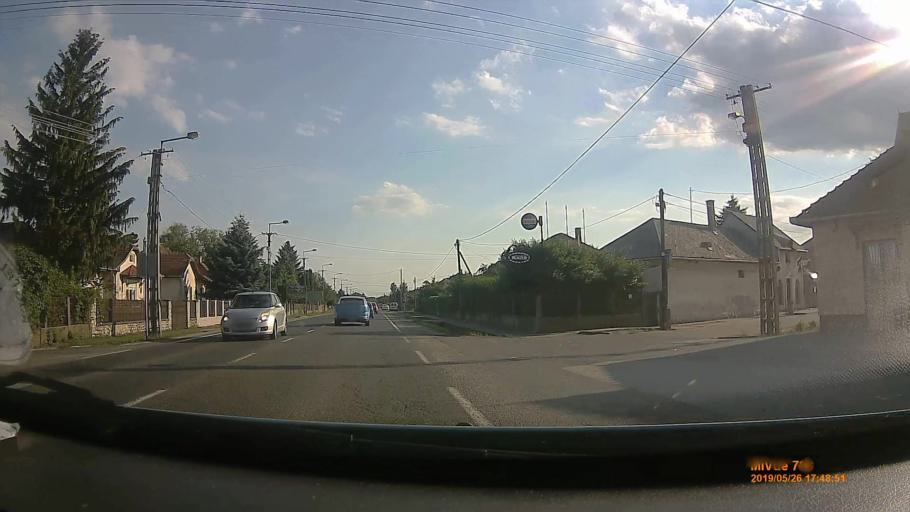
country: HU
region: Borsod-Abauj-Zemplen
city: Szikszo
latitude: 48.1929
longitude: 20.9279
